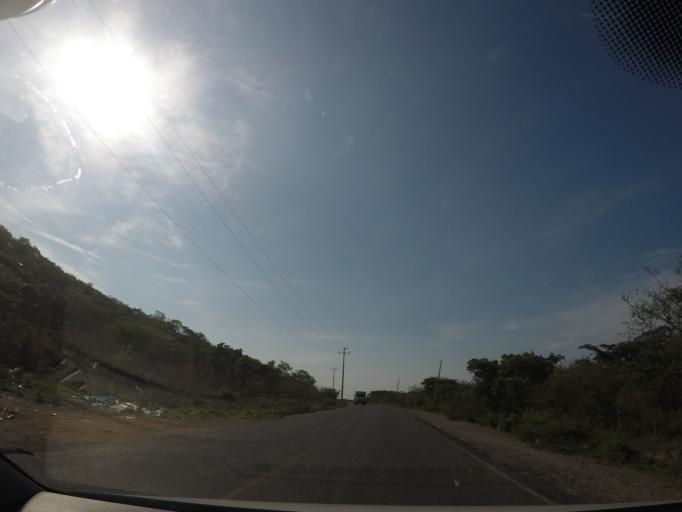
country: MX
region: Oaxaca
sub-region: Salina Cruz
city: Salina Cruz
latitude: 16.2293
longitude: -95.1407
